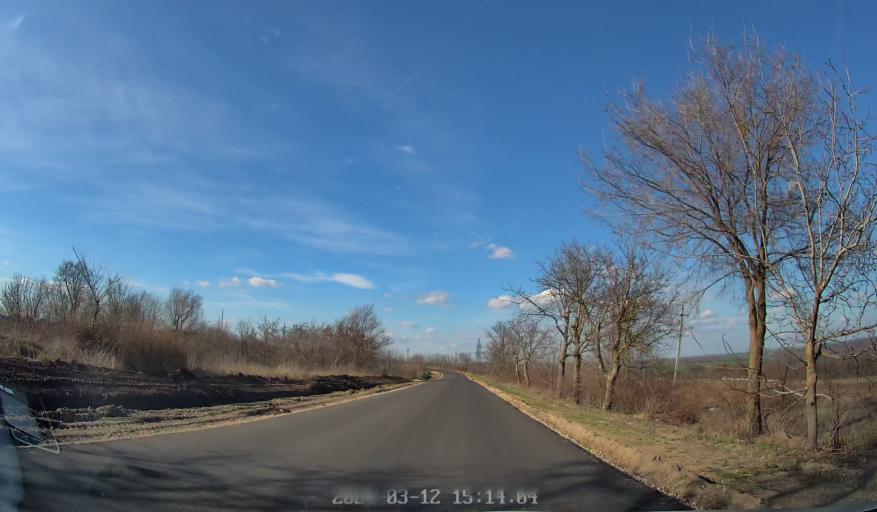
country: MD
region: Chisinau
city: Ciorescu
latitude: 47.2328
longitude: 28.9551
